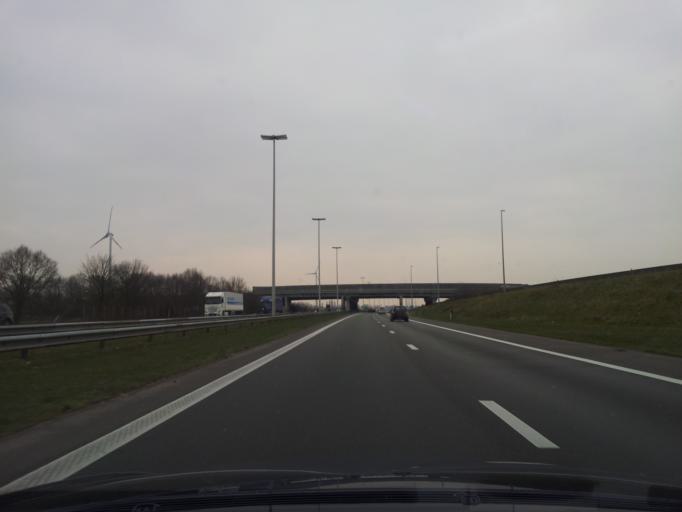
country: BE
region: Flanders
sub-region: Provincie Antwerpen
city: Hoogstraten
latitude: 51.4157
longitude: 4.7036
